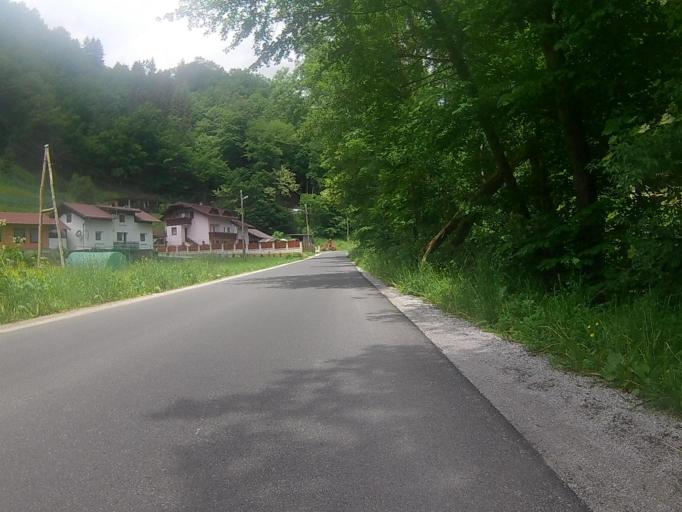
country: SI
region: Maribor
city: Bresternica
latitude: 46.5921
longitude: 15.5556
